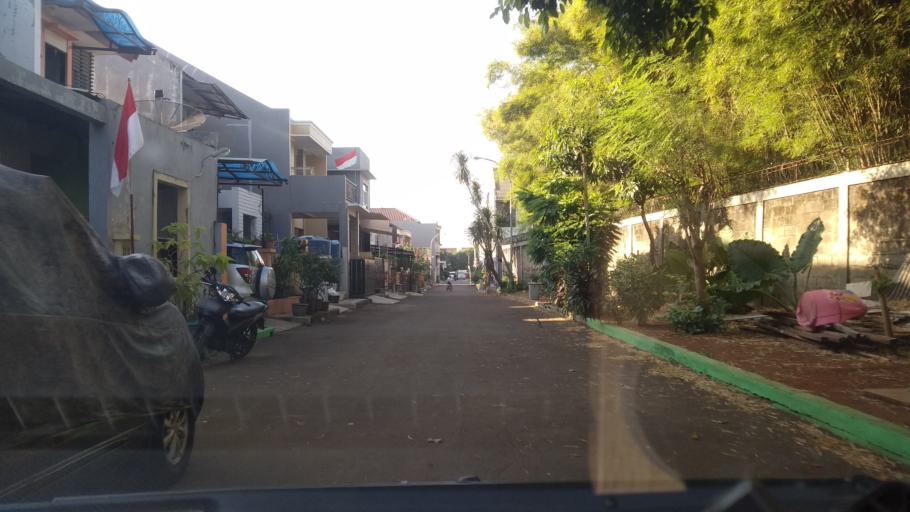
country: ID
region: Banten
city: South Tangerang
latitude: -6.2599
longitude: 106.7378
